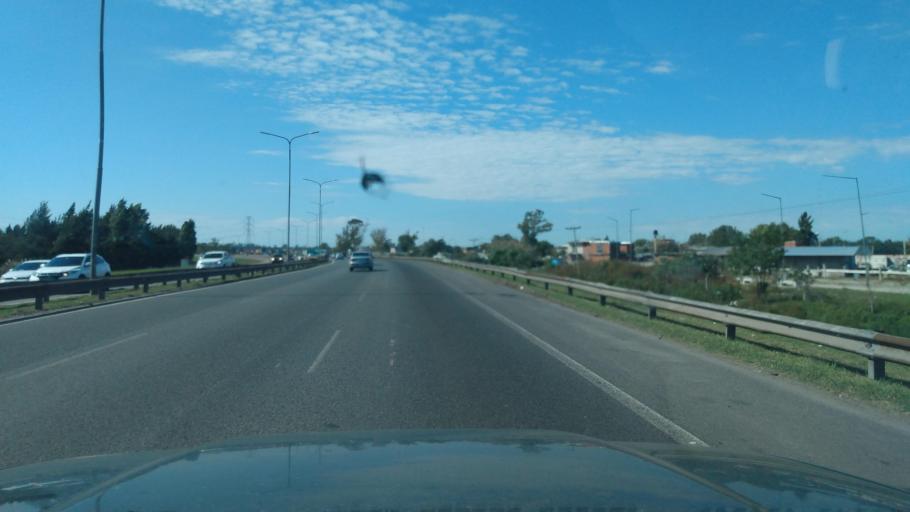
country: AR
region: Buenos Aires
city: Hurlingham
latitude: -34.5516
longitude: -58.6141
